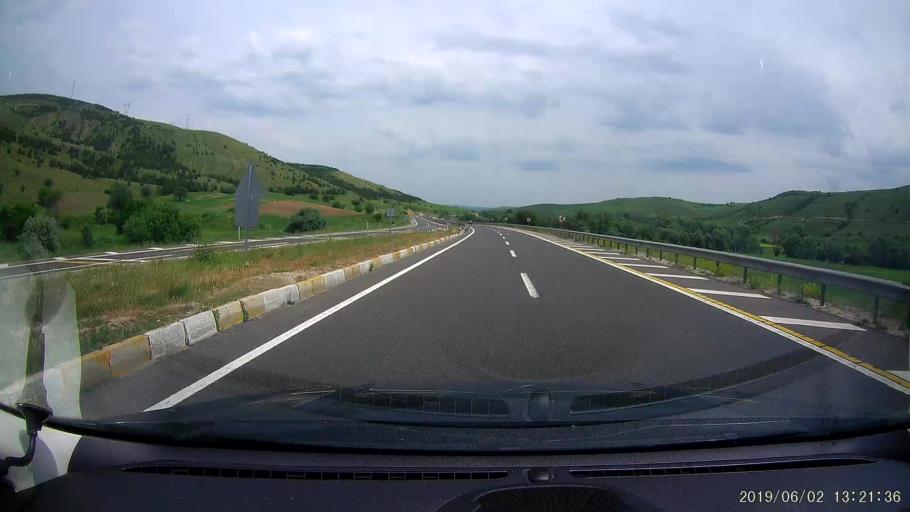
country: TR
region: Cankiri
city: Cerkes
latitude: 40.8311
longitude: 32.7768
